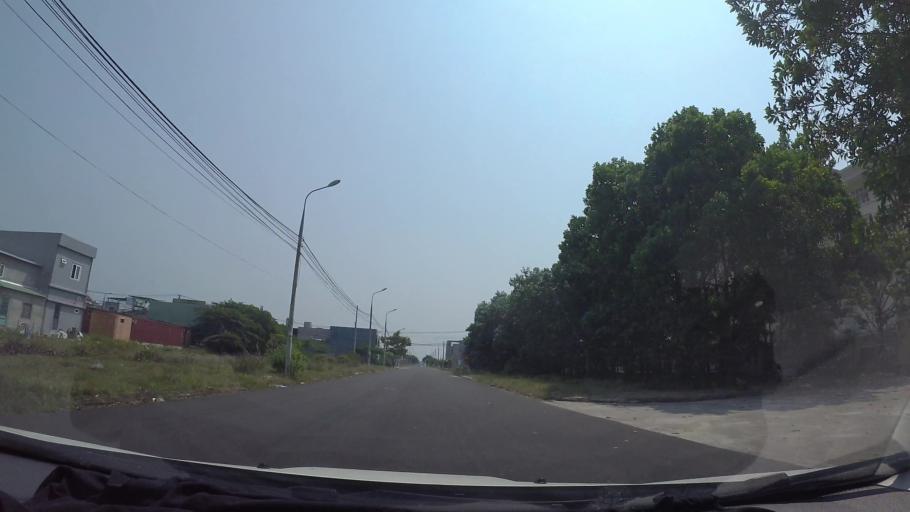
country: VN
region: Da Nang
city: Cam Le
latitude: 15.9823
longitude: 108.2114
